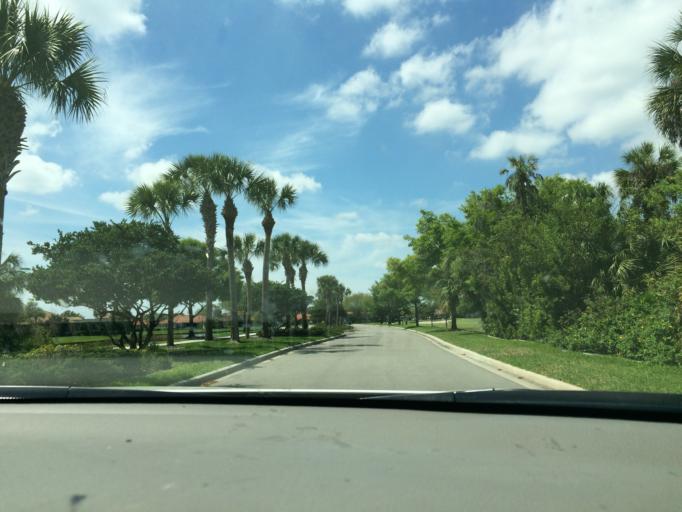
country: US
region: Florida
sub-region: Manatee County
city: Ellenton
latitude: 27.5085
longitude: -82.4377
